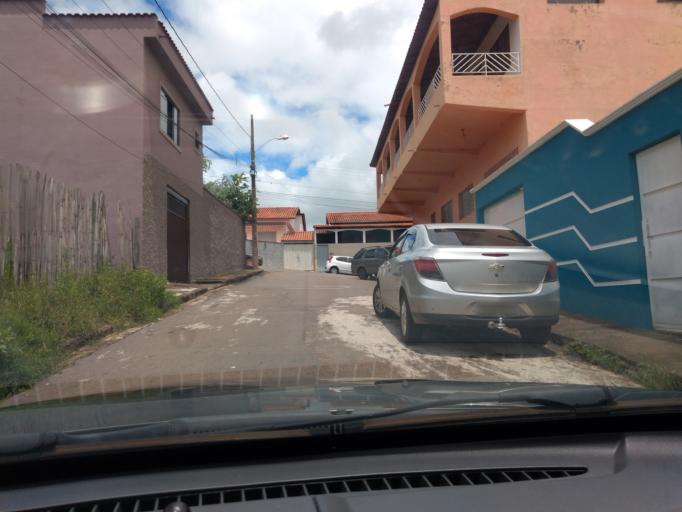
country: BR
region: Minas Gerais
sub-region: Tres Coracoes
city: Tres Coracoes
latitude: -21.6895
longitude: -45.2538
